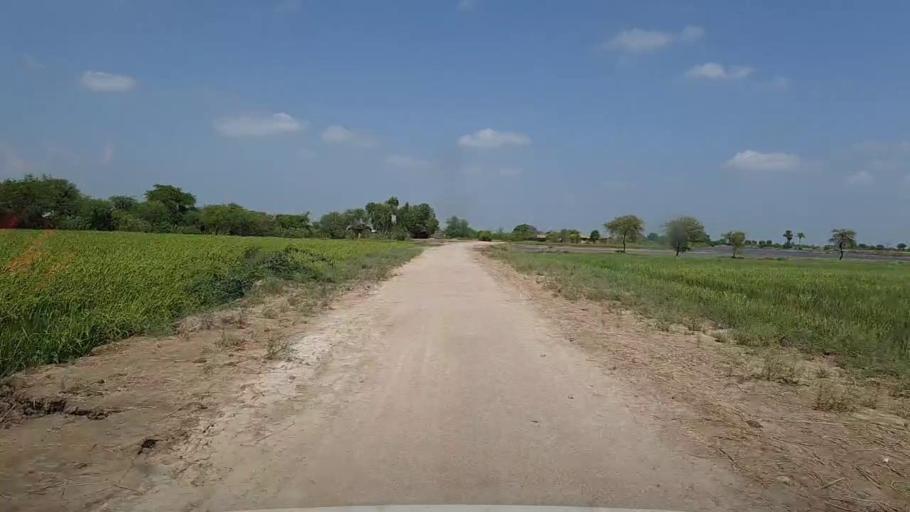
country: PK
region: Sindh
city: Kario
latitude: 24.6920
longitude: 68.5880
